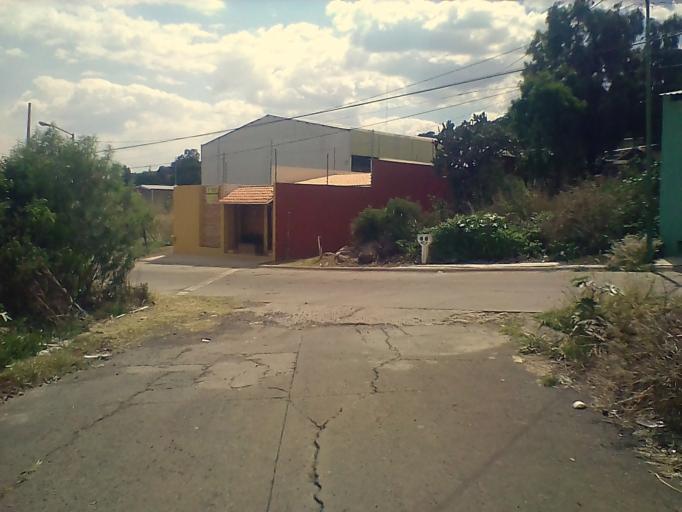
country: MX
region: Michoacan
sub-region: Tarimbaro
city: Fraccionamiento Metropolis II
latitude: 19.7140
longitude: -101.2385
